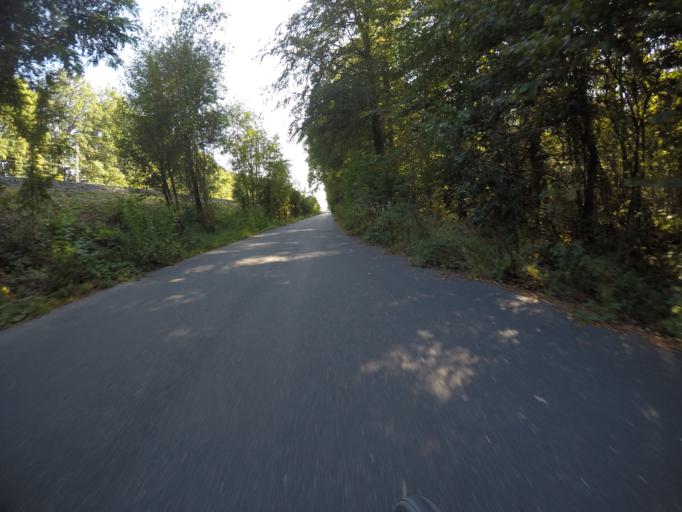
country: DE
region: Hesse
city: Dreieich
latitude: 50.0263
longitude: 8.6614
